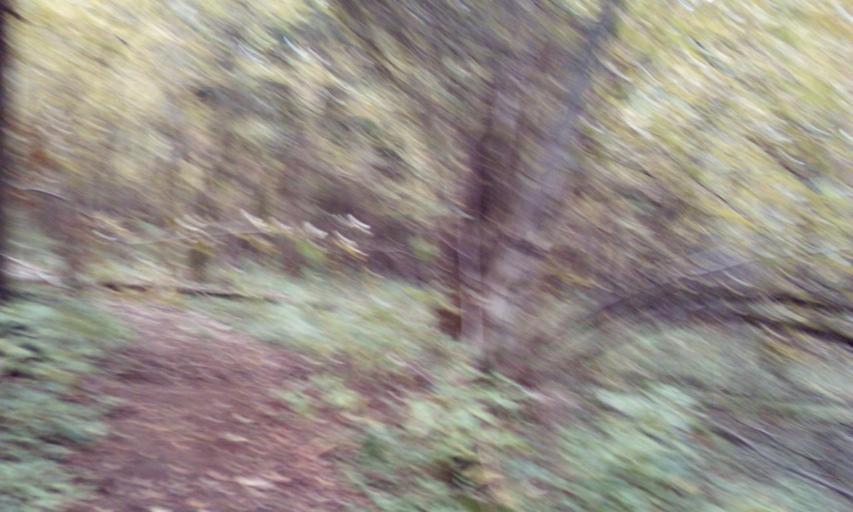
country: RU
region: Moskovskaya
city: Gorki Vtoryye
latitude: 55.6950
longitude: 37.1853
